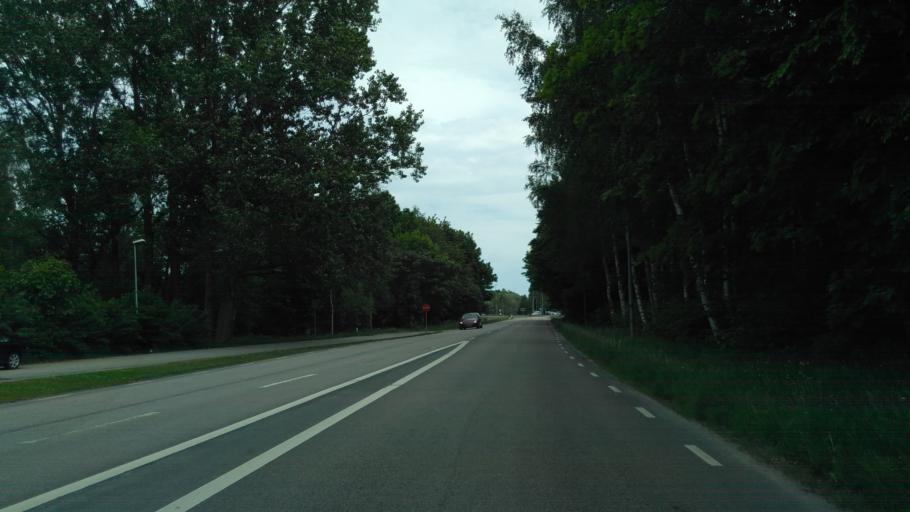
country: SE
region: Vaestra Goetaland
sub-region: Lidkopings Kommun
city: Lidkoping
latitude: 58.4893
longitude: 13.1430
